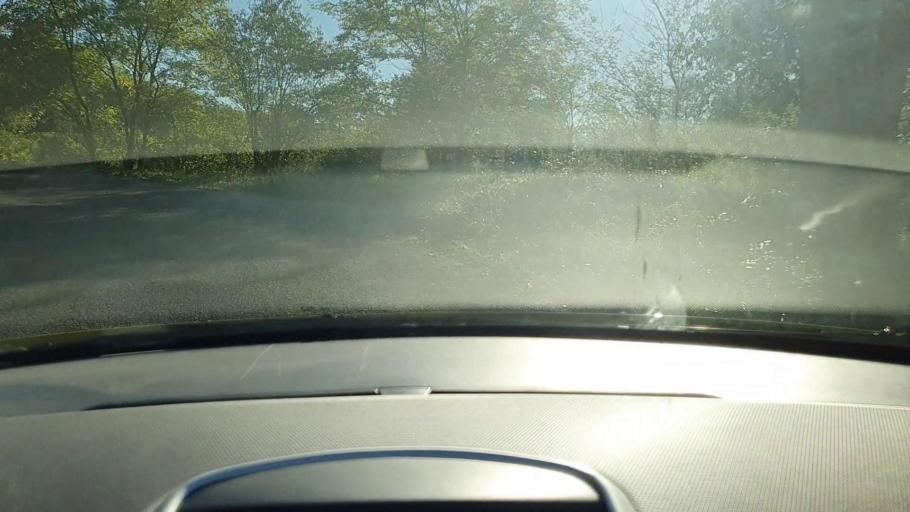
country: FR
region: Languedoc-Roussillon
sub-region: Departement du Gard
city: Valleraugue
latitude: 44.0355
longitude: 3.6822
